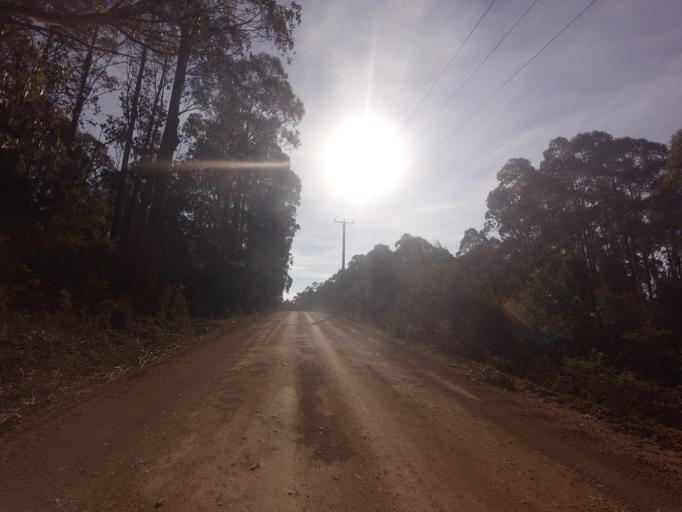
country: AU
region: Tasmania
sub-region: Sorell
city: Sorell
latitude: -42.5035
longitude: 147.5438
